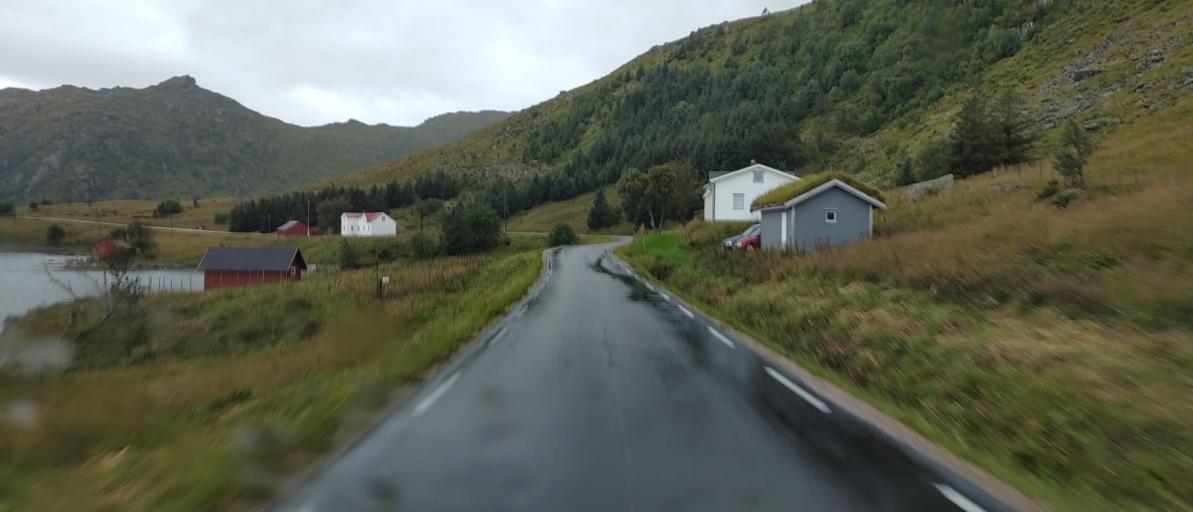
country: NO
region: Nordland
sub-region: Vestvagoy
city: Evjen
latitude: 68.2847
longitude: 13.7192
